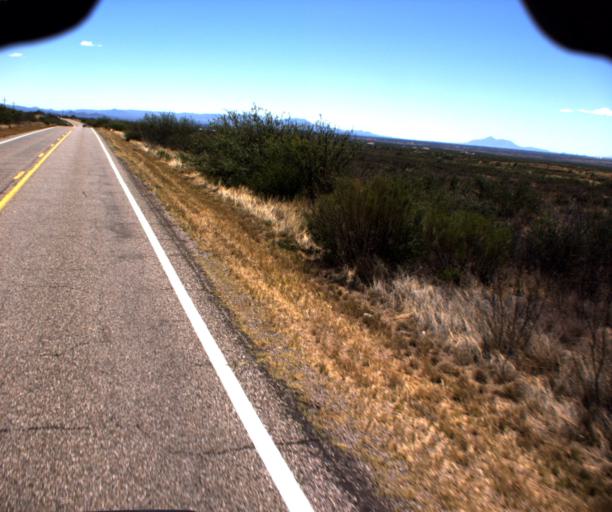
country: US
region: Arizona
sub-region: Cochise County
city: Huachuca City
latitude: 31.6929
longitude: -110.4073
